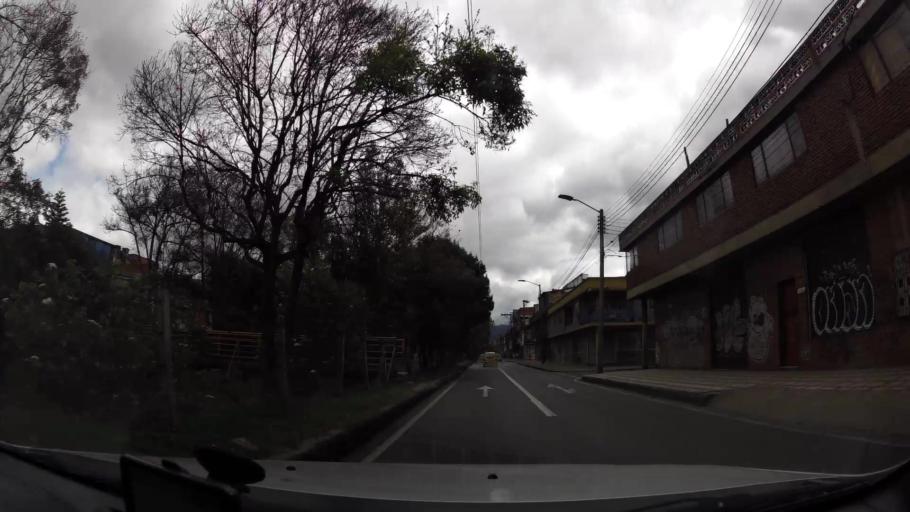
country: CO
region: Bogota D.C.
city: Bogota
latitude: 4.6188
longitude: -74.1189
